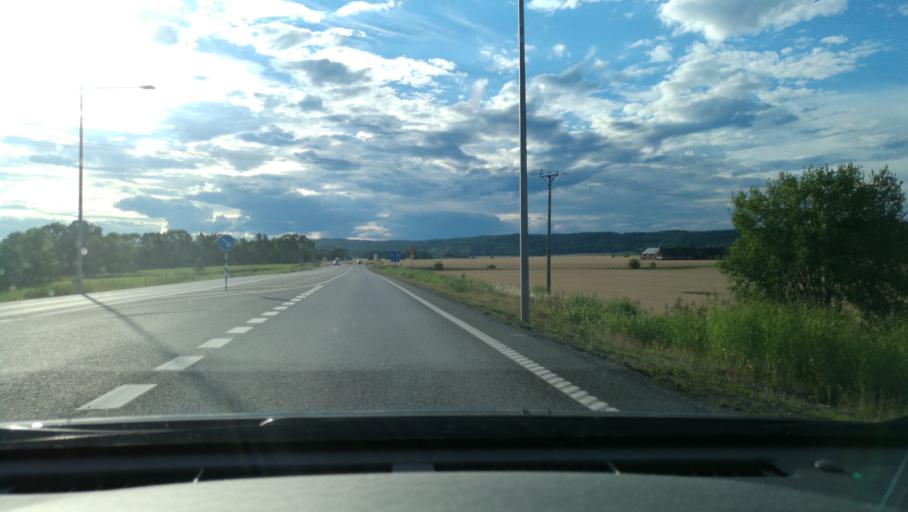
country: SE
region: OEstergoetland
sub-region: Norrkopings Kommun
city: Norrkoping
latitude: 58.6293
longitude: 16.1471
